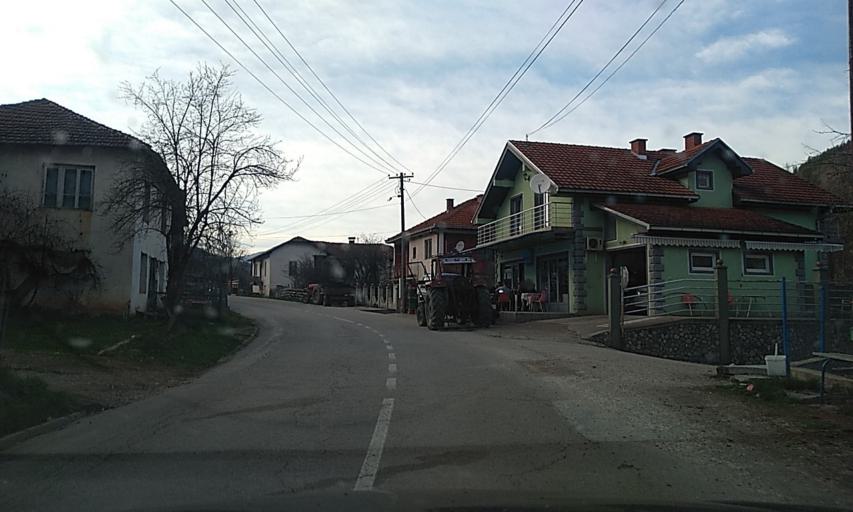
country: RS
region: Central Serbia
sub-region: Pcinjski Okrug
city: Bosilegrad
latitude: 42.4636
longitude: 22.4890
